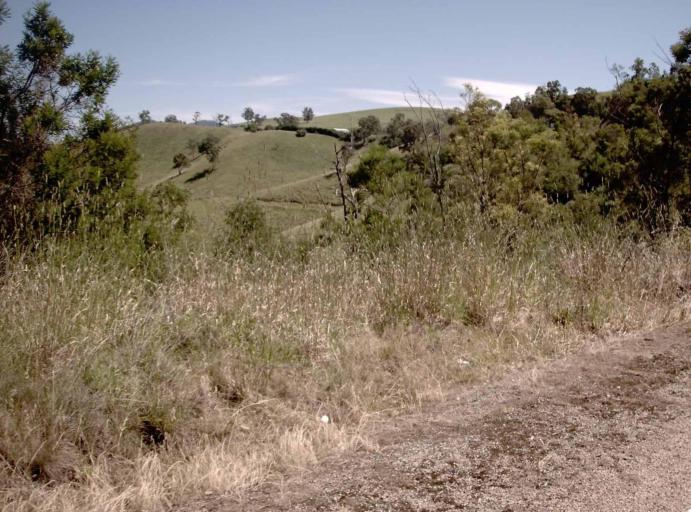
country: AU
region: Victoria
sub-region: East Gippsland
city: Lakes Entrance
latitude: -37.4895
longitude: 148.1863
